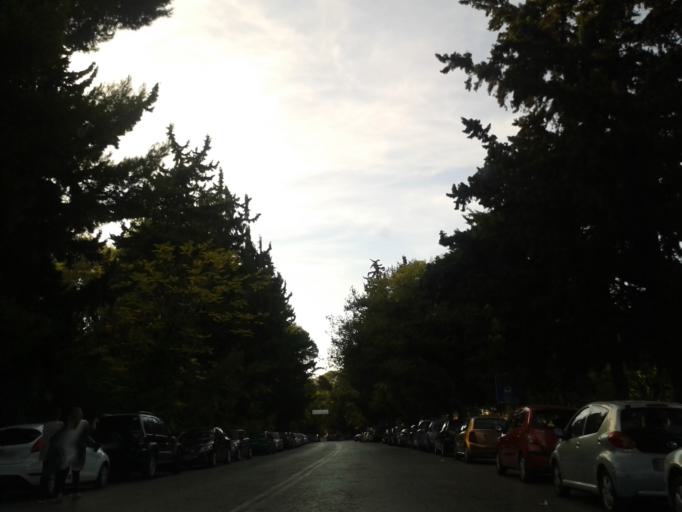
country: GR
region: Attica
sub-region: Nomarchia Athinas
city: Chaidari
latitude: 38.0116
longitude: 23.6420
